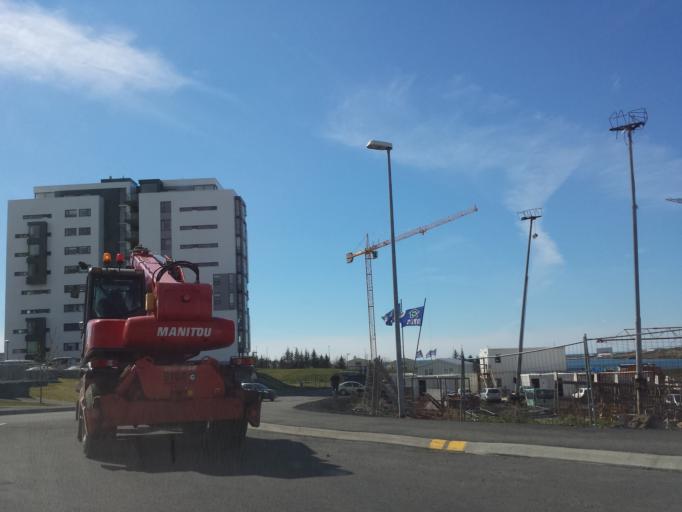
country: IS
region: Capital Region
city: Reykjavik
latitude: 64.1158
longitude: -21.8933
